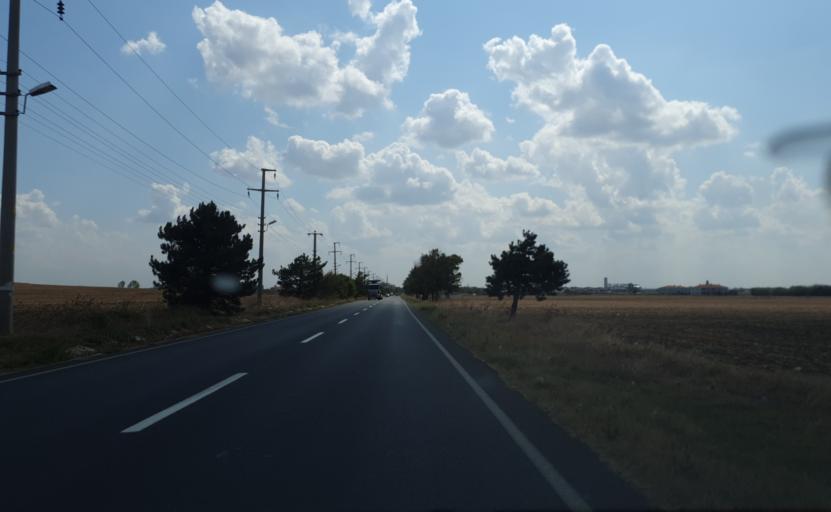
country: TR
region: Kirklareli
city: Luleburgaz
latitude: 41.3705
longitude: 27.3401
